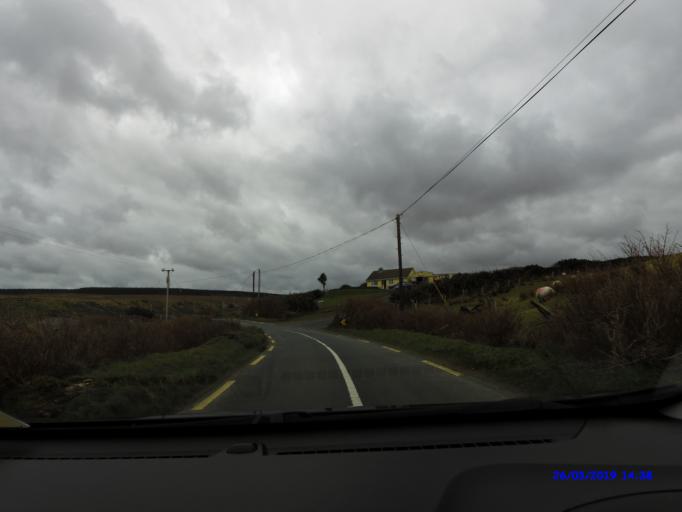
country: IE
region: Connaught
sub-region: Maigh Eo
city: Crossmolina
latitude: 54.3094
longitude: -9.5050
